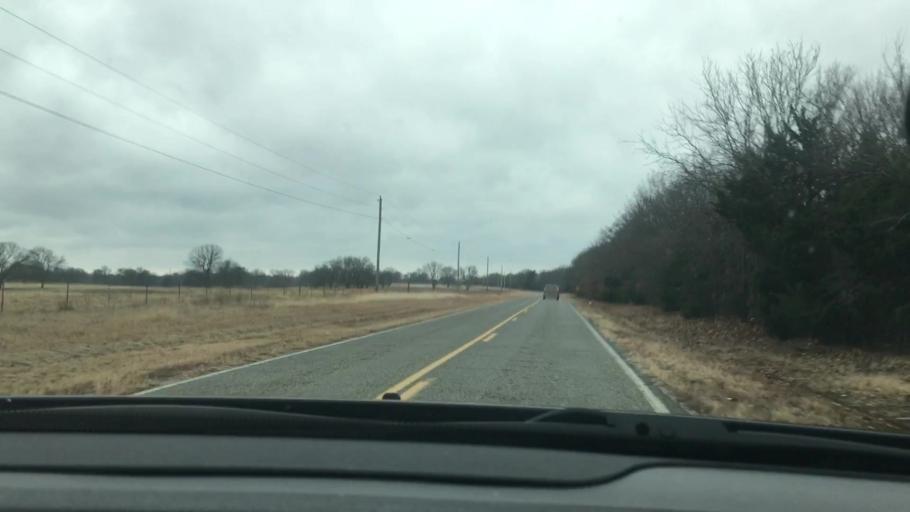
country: US
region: Oklahoma
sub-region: Johnston County
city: Tishomingo
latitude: 34.1940
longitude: -96.5782
